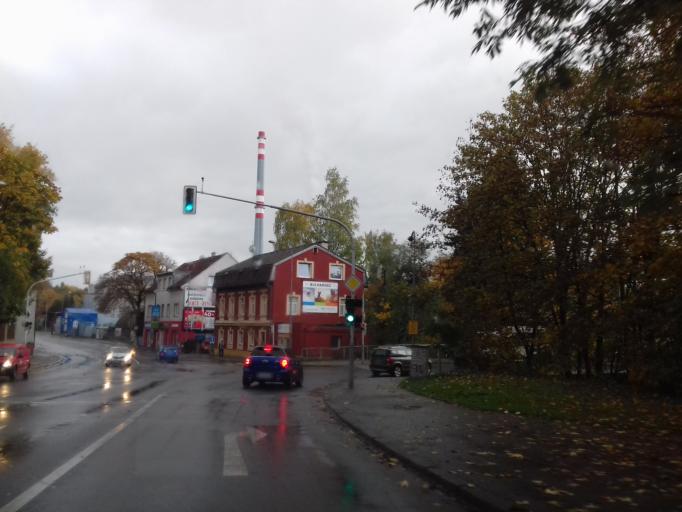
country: CZ
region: Liberecky
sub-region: Okres Liberec
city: Liberec
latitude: 50.7610
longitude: 15.0543
